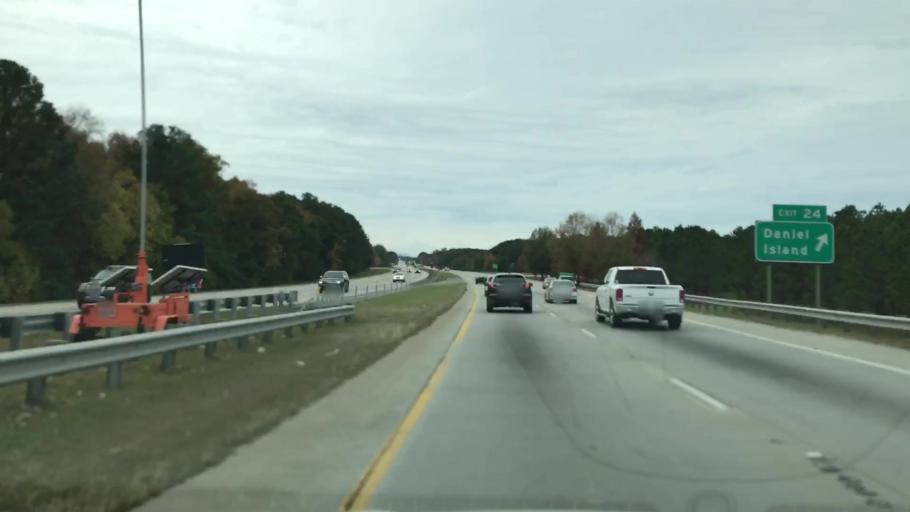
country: US
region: South Carolina
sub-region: Charleston County
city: North Charleston
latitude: 32.8662
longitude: -79.9060
